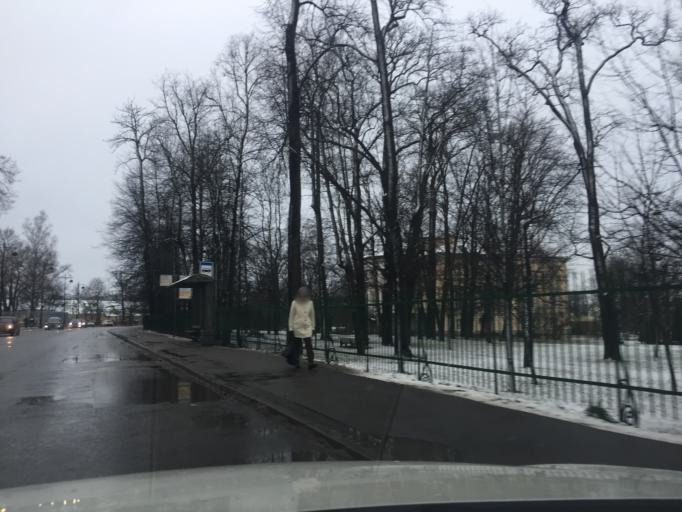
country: RU
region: St.-Petersburg
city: Pushkin
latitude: 59.7122
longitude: 30.4107
